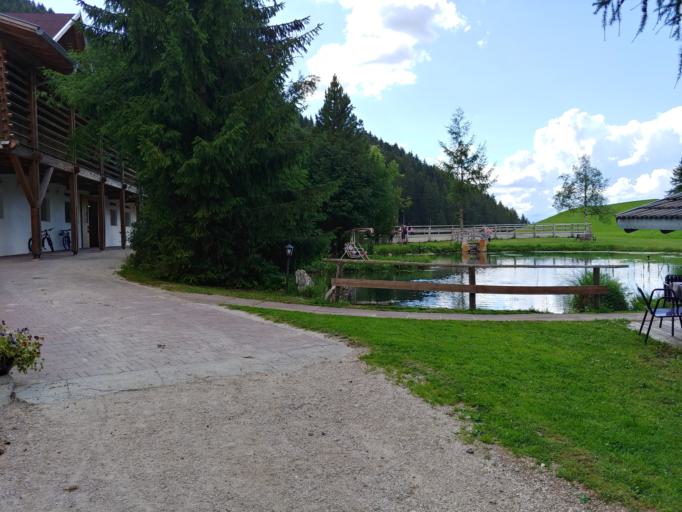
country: IT
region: Trentino-Alto Adige
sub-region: Bolzano
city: Santa Cristina Valgardena
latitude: 46.5527
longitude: 11.7411
